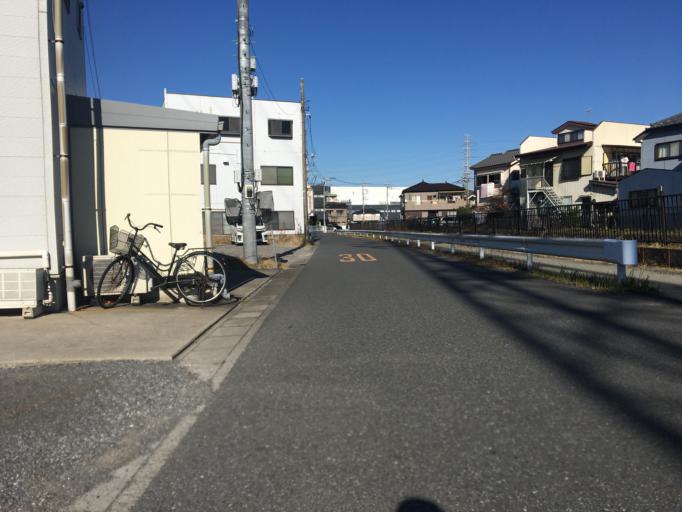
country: JP
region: Saitama
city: Yashio-shi
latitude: 35.8343
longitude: 139.8315
